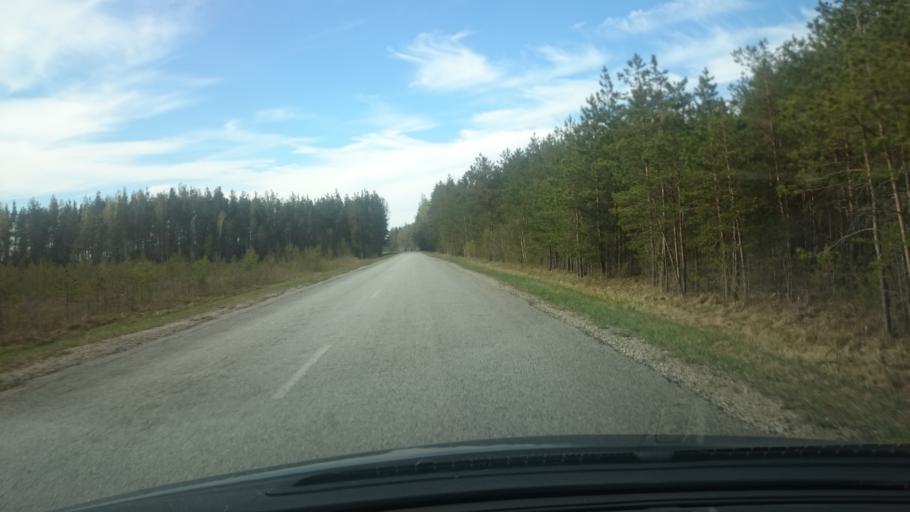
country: EE
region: Ida-Virumaa
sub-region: Toila vald
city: Voka
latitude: 59.1072
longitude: 27.6435
